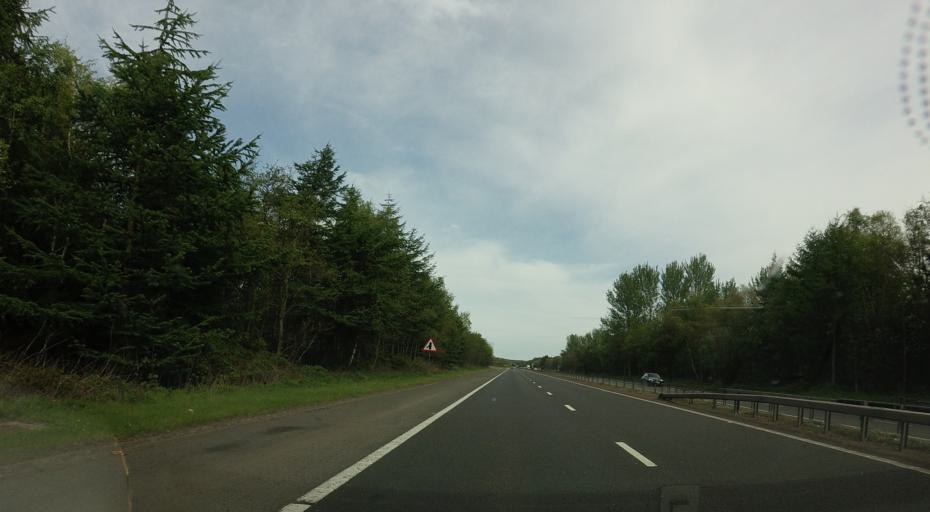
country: GB
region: Scotland
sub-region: West Lothian
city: Linlithgow
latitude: 55.9881
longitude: -3.5635
